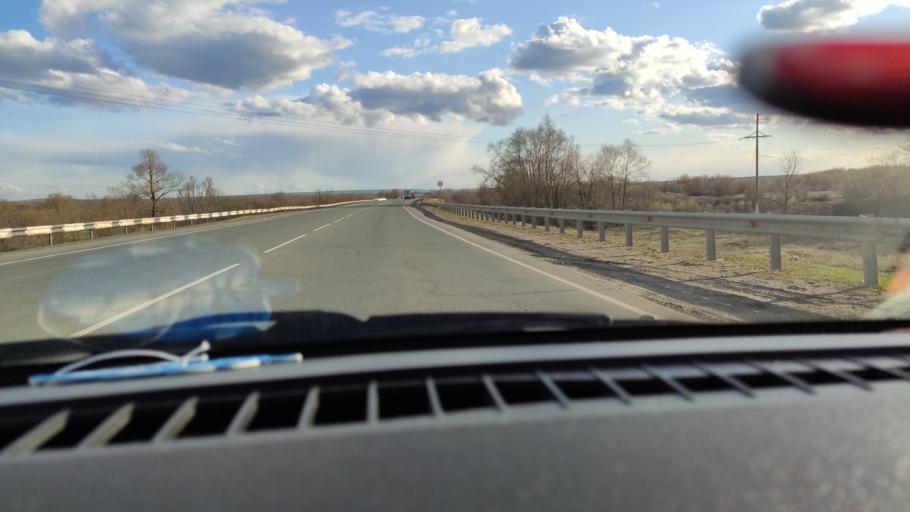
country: RU
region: Saratov
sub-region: Saratovskiy Rayon
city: Saratov
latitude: 51.7252
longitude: 46.0290
